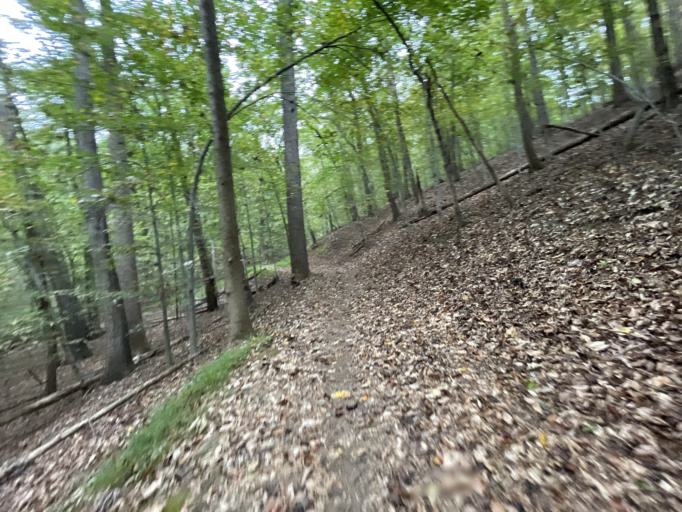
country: US
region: Maryland
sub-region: Baltimore County
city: Hampton
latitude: 39.4313
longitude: -76.5690
